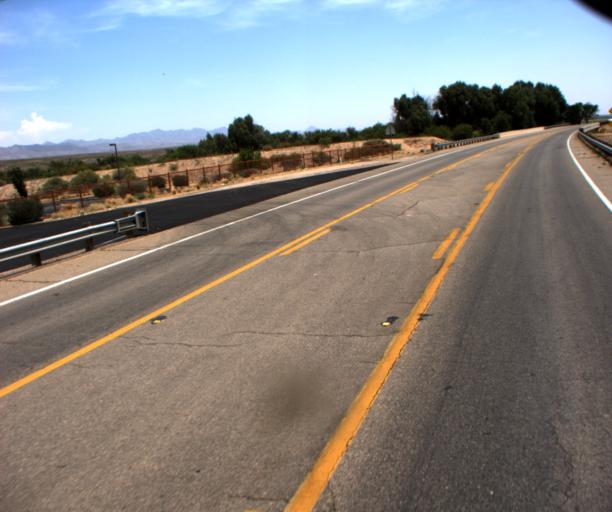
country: US
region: Arizona
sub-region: Graham County
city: Bylas
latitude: 33.0356
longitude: -109.9619
